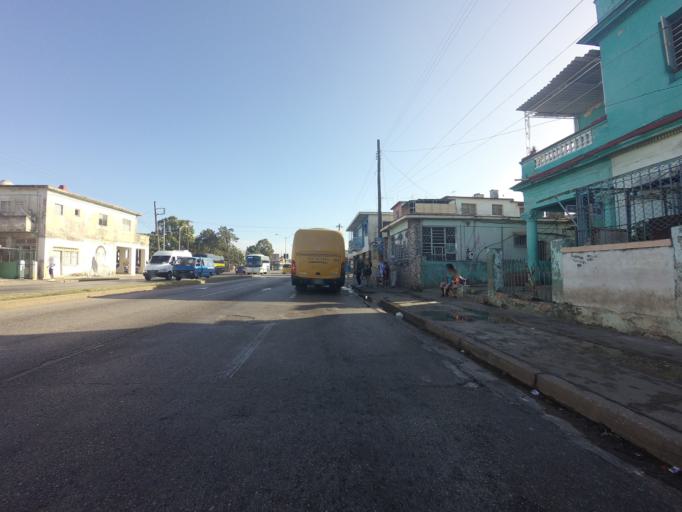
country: CU
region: La Habana
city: Cerro
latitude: 23.1025
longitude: -82.4296
